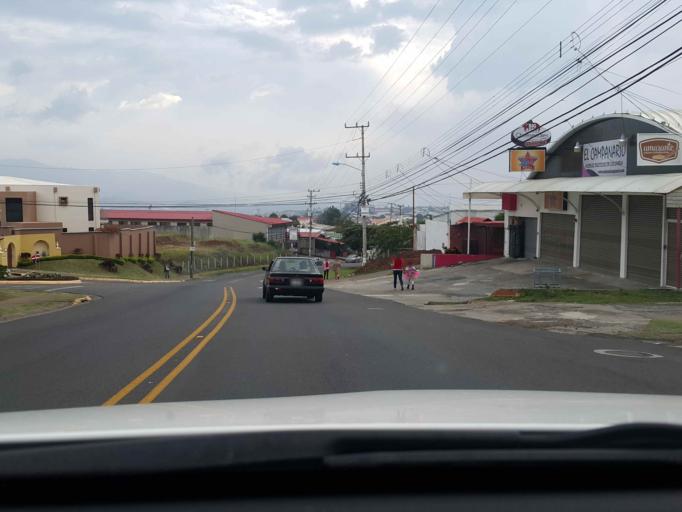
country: CR
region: Heredia
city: San Pablo
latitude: 9.9997
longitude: -84.1044
